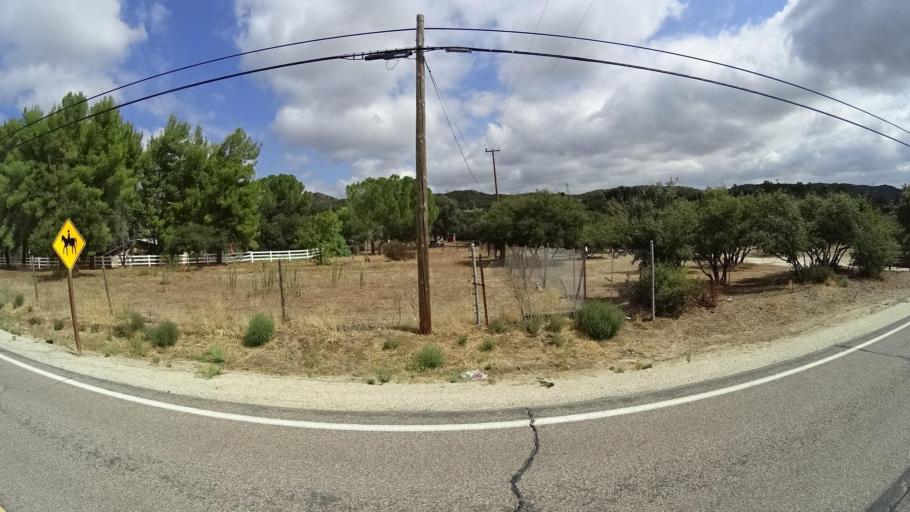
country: US
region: California
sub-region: San Diego County
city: Campo
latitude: 32.6717
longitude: -116.4885
